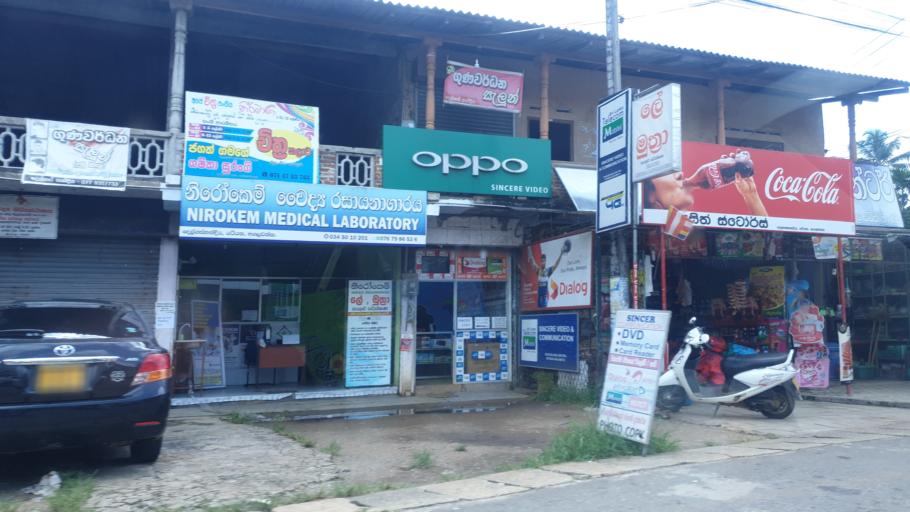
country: LK
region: Western
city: Horawala Junction
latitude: 6.5336
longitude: 80.1368
